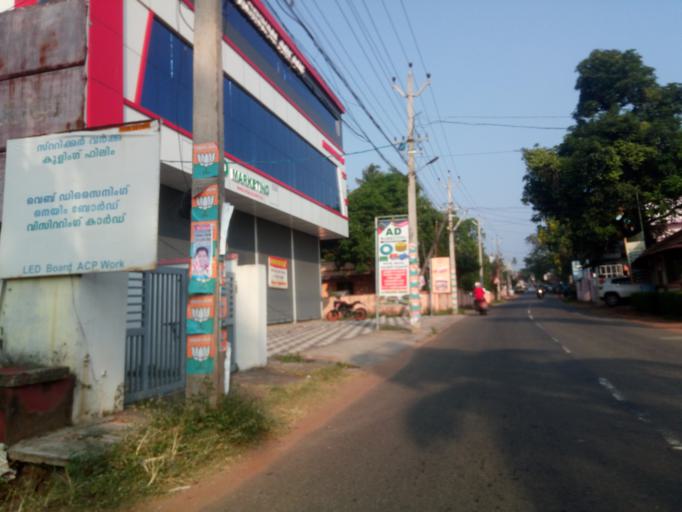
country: IN
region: Kerala
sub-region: Thrissur District
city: Irinjalakuda
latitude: 10.3430
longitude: 76.2140
